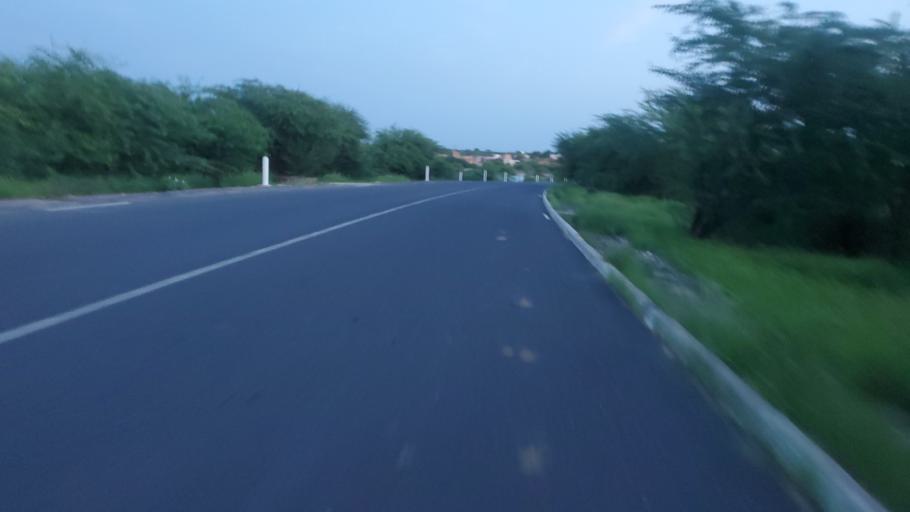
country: SN
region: Saint-Louis
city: Saint-Louis
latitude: 16.0748
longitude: -16.3892
